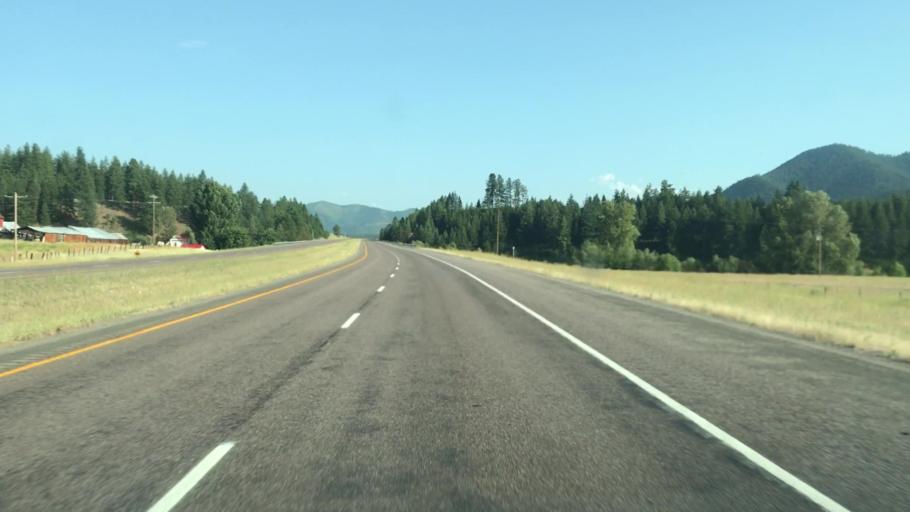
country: US
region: Montana
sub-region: Mineral County
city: Superior
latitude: 47.0552
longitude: -114.7607
